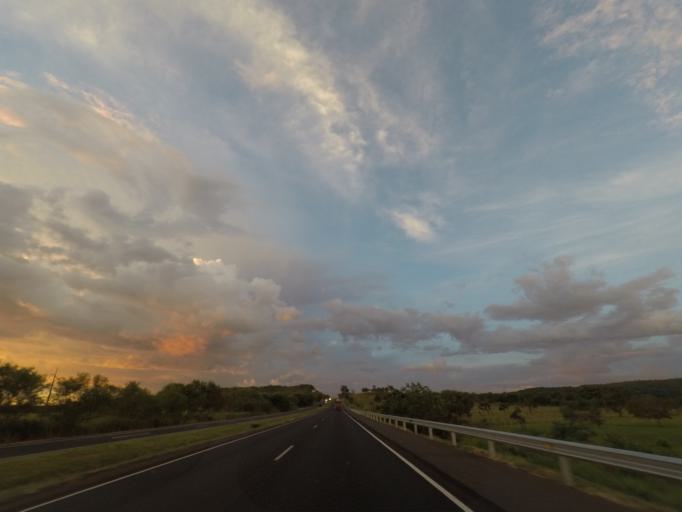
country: BR
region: Minas Gerais
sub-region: Uberaba
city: Uberaba
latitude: -19.6007
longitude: -48.0249
